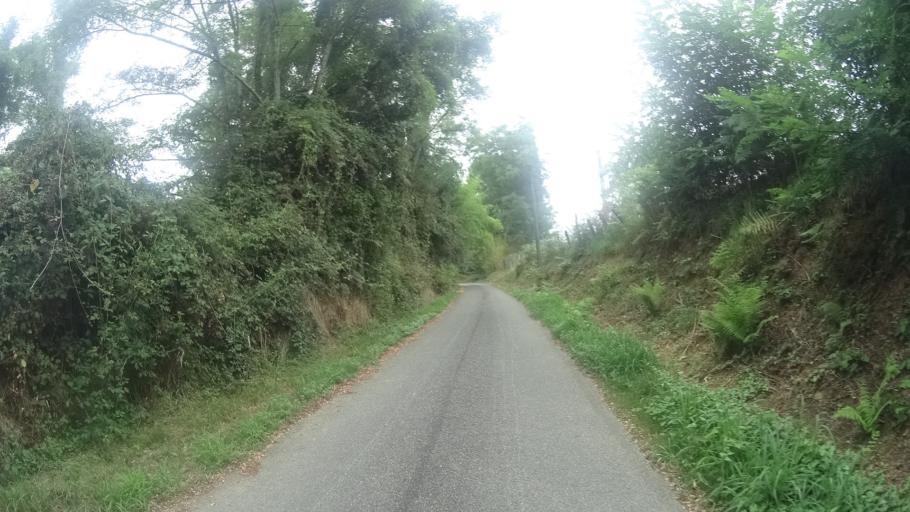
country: FR
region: Aquitaine
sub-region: Departement des Pyrenees-Atlantiques
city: Mont
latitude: 43.4852
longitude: -0.6877
